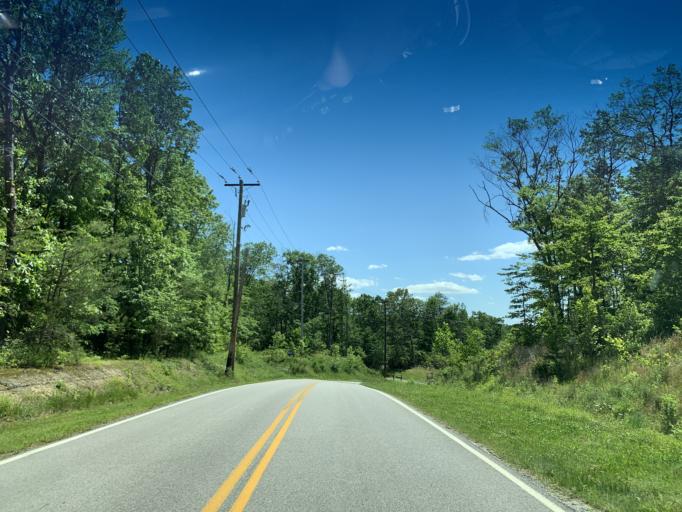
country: US
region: Maryland
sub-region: Cecil County
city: Charlestown
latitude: 39.5224
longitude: -75.9398
